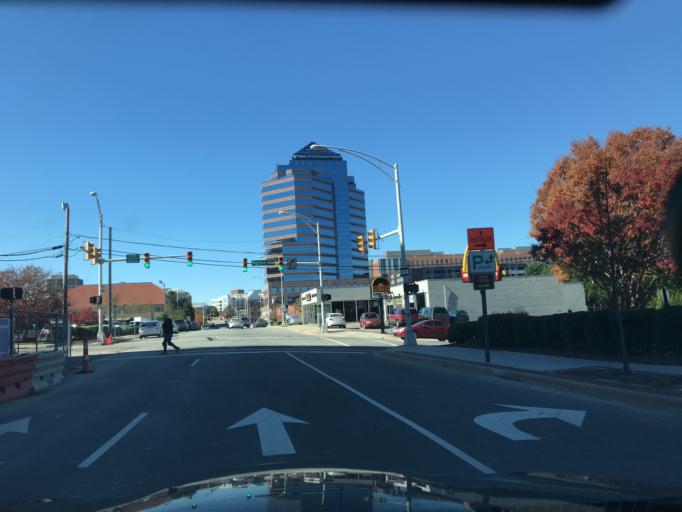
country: US
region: North Carolina
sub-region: Durham County
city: Durham
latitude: 35.9980
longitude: -78.8995
